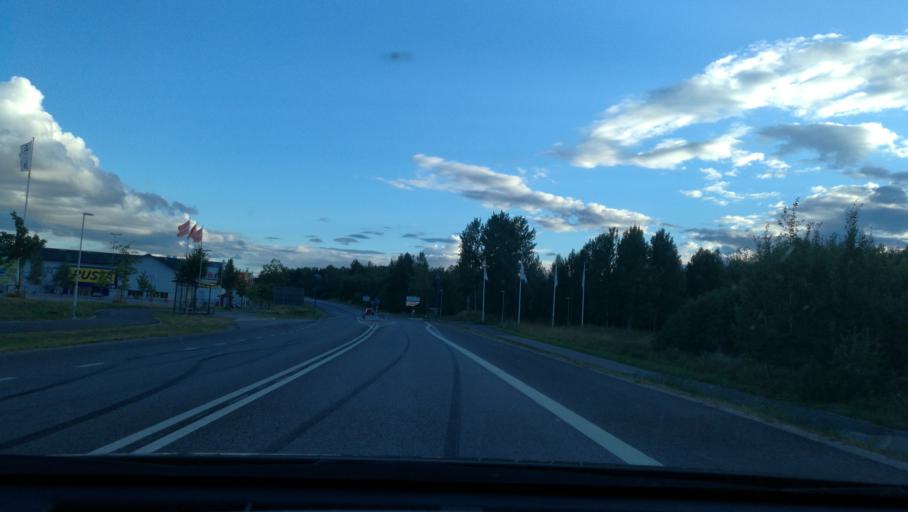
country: SE
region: Soedermanland
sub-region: Katrineholms Kommun
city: Katrineholm
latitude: 59.0049
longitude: 16.2268
